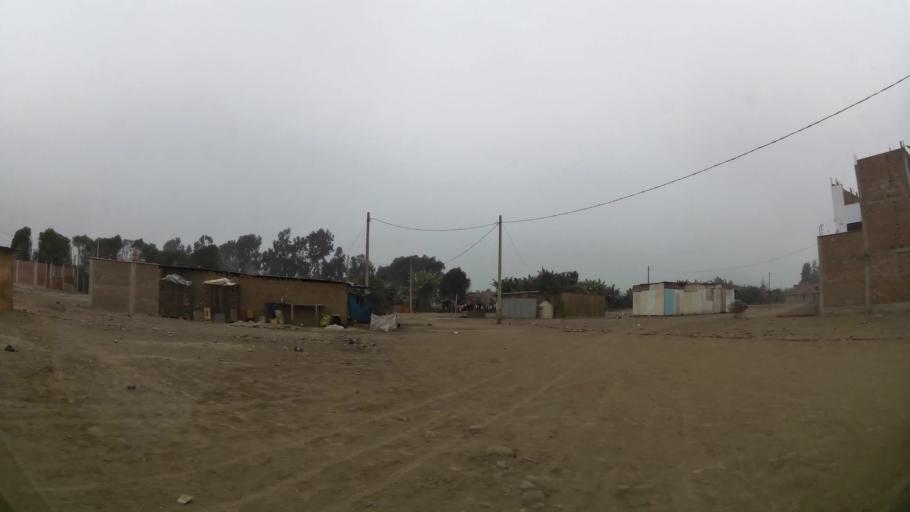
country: PE
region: Lima
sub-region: Lima
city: Carabayllo
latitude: -11.8573
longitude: -77.0197
